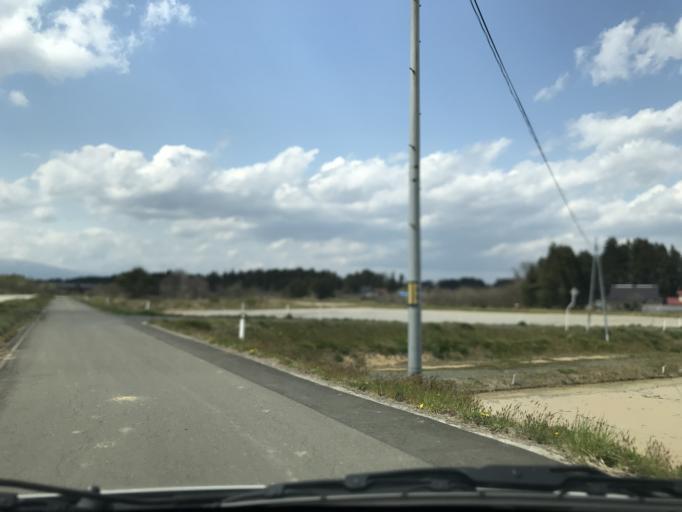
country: JP
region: Iwate
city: Mizusawa
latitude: 39.0700
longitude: 141.1052
